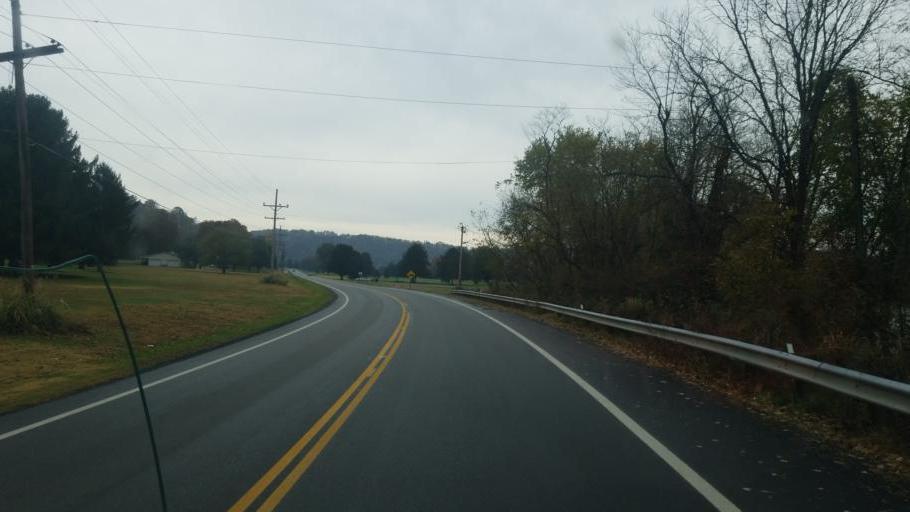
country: US
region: Ohio
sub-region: Washington County
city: Beverly
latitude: 39.5510
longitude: -81.6068
